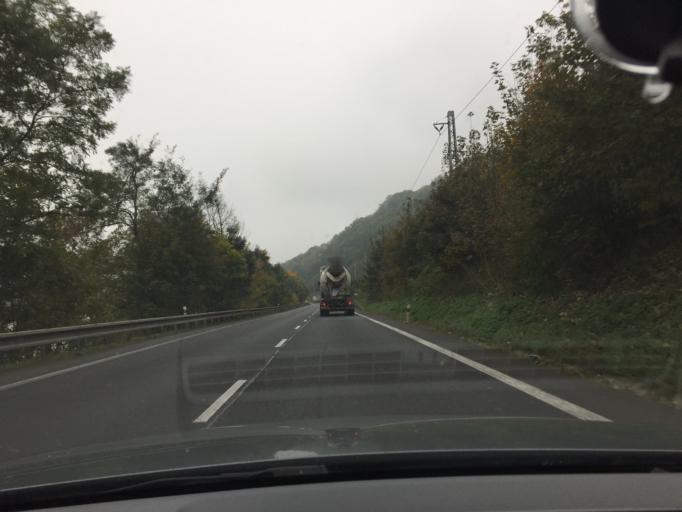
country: CZ
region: Ustecky
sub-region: Okres Usti nad Labem
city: Usti nad Labem
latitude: 50.6087
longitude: 14.0733
